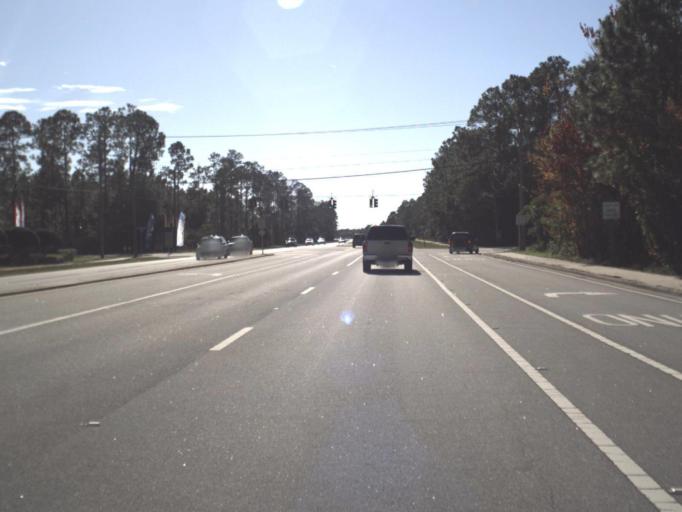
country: US
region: Florida
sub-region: Volusia County
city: Holly Hill
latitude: 29.2381
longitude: -81.0914
